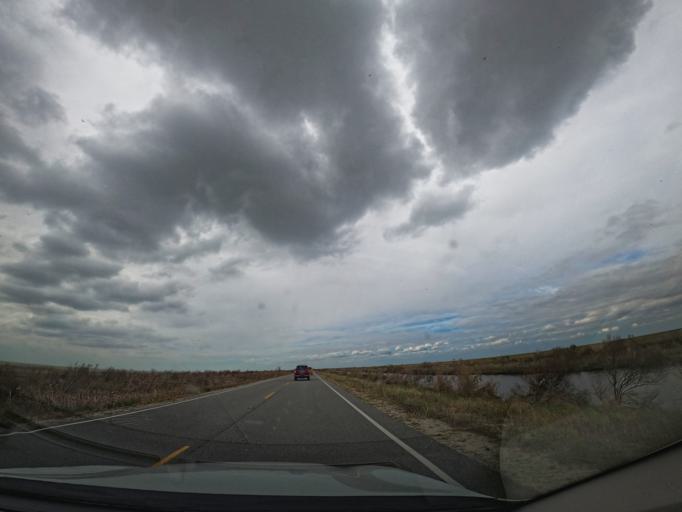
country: US
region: Louisiana
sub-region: Cameron Parish
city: Cameron
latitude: 29.7674
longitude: -93.3917
